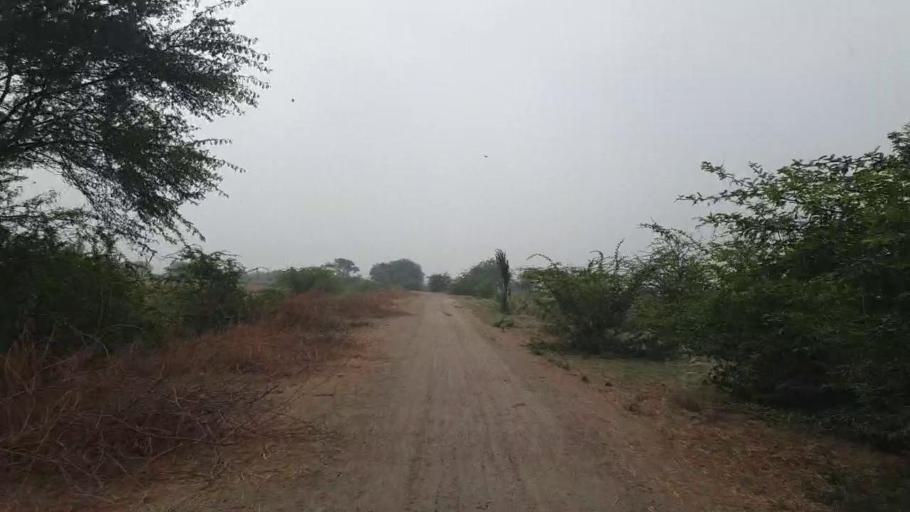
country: PK
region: Sindh
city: Badin
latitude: 24.5885
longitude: 68.6795
